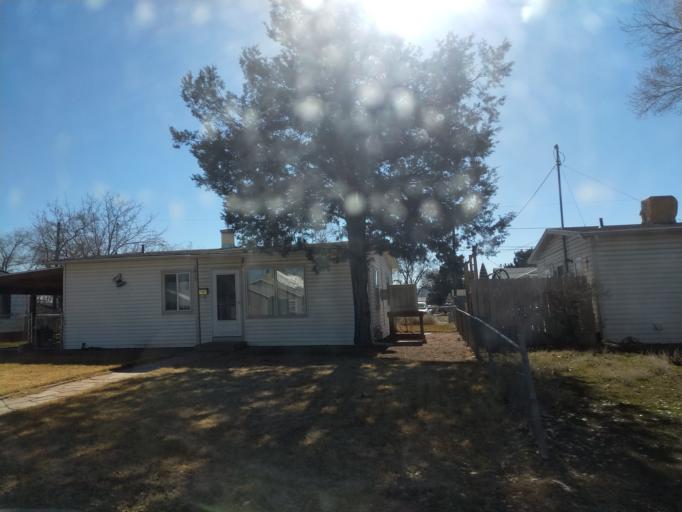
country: US
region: Colorado
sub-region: Mesa County
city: Grand Junction
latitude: 39.0701
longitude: -108.5428
